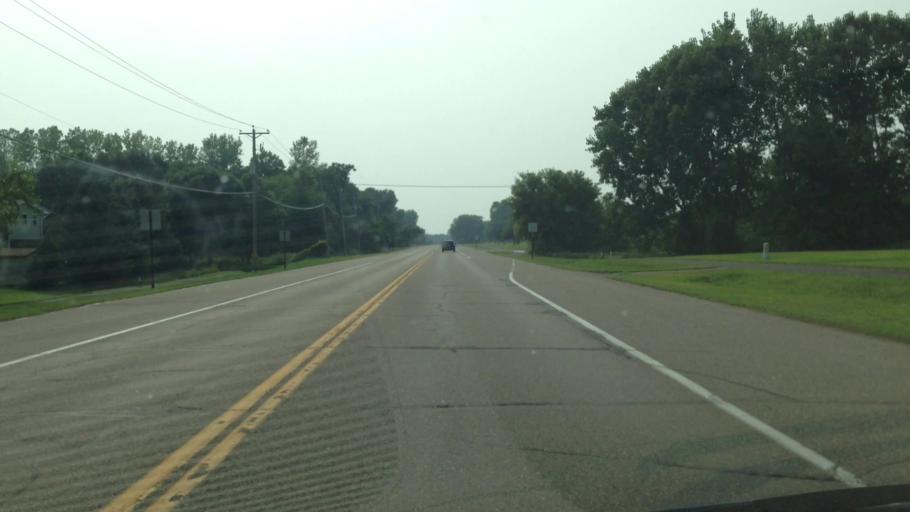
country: US
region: Minnesota
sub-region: Anoka County
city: Lino Lakes
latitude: 45.1422
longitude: -93.1099
